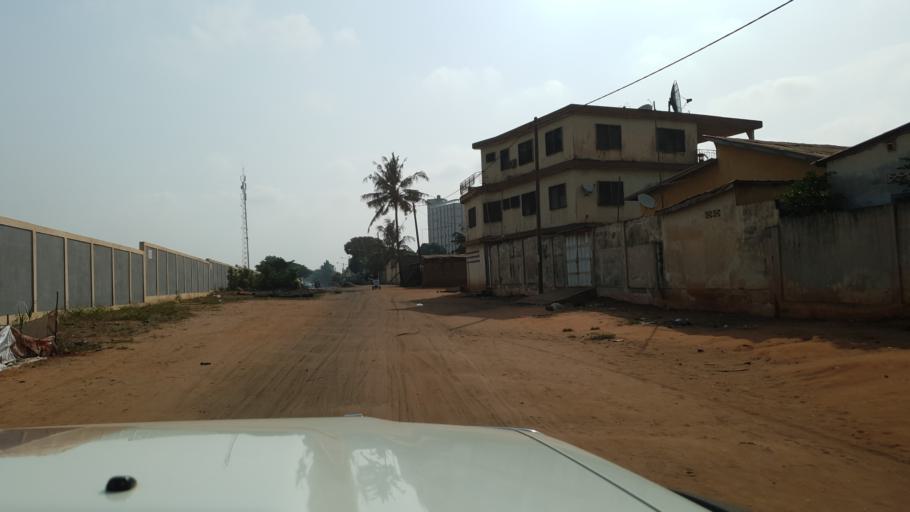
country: TG
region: Maritime
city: Lome
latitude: 6.1651
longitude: 1.2121
